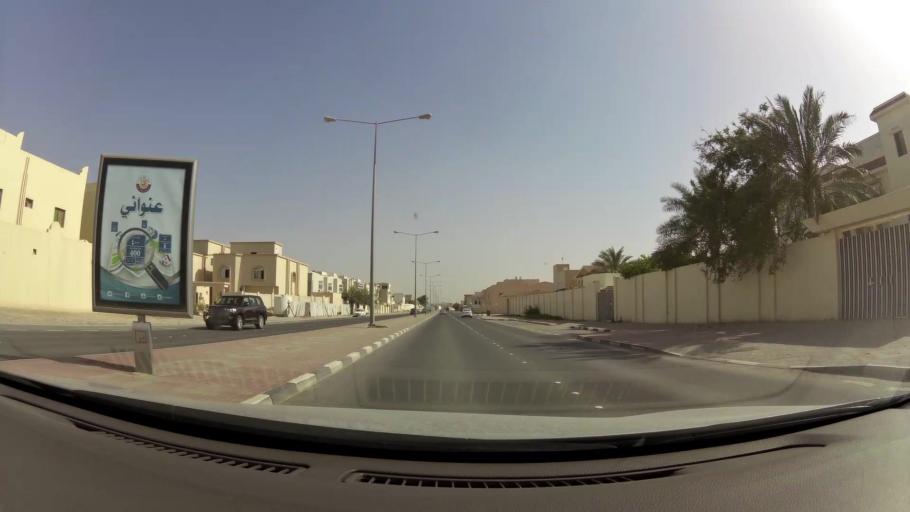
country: QA
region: Baladiyat Umm Salal
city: Umm Salal Muhammad
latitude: 25.3622
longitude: 51.4368
